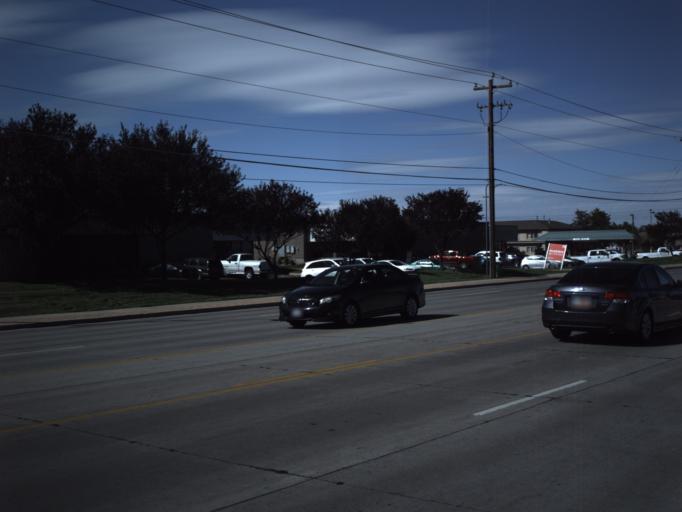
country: US
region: Utah
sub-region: Salt Lake County
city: Taylorsville
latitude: 40.7098
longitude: -111.9388
